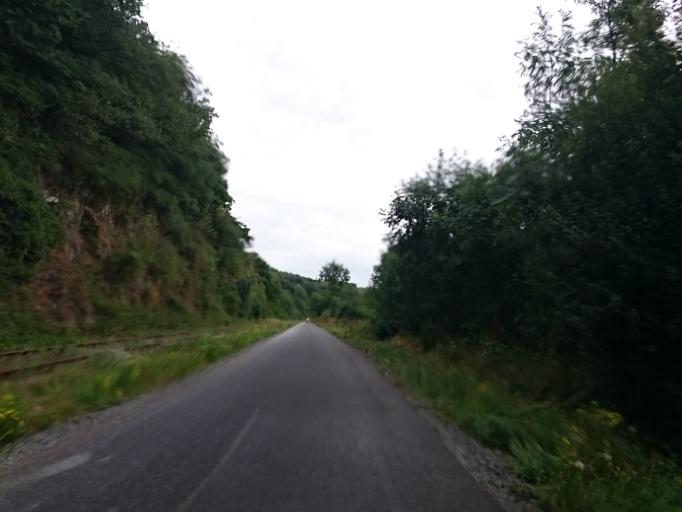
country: FR
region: Lower Normandy
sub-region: Departement du Calvados
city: Sainte-Honorine-du-Fay
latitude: 49.0519
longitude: -0.4584
